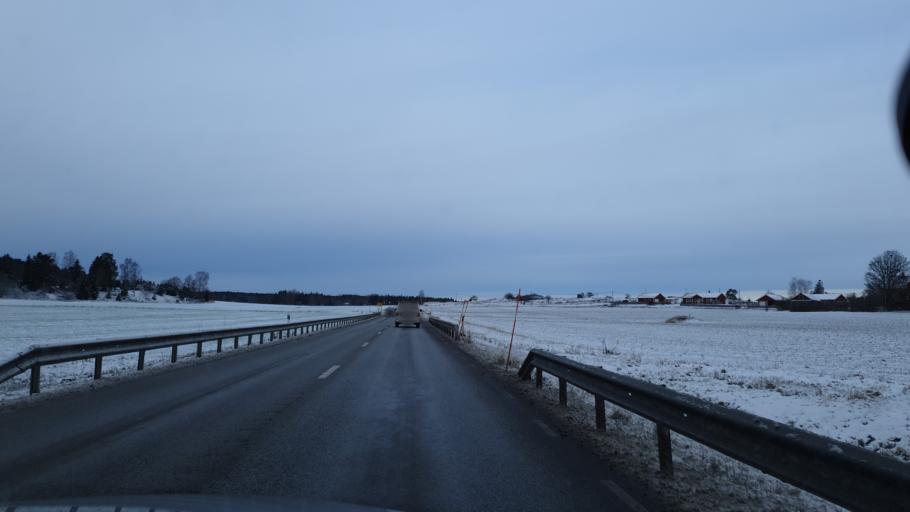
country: SE
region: Uppsala
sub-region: Habo Kommun
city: Balsta
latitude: 59.6219
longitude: 17.6055
